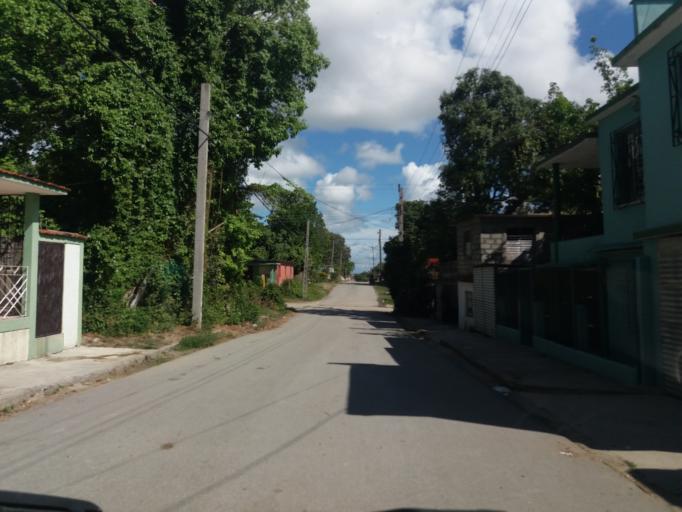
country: CU
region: Cienfuegos
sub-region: Municipio de Cienfuegos
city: Cienfuegos
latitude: 22.1476
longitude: -80.4237
